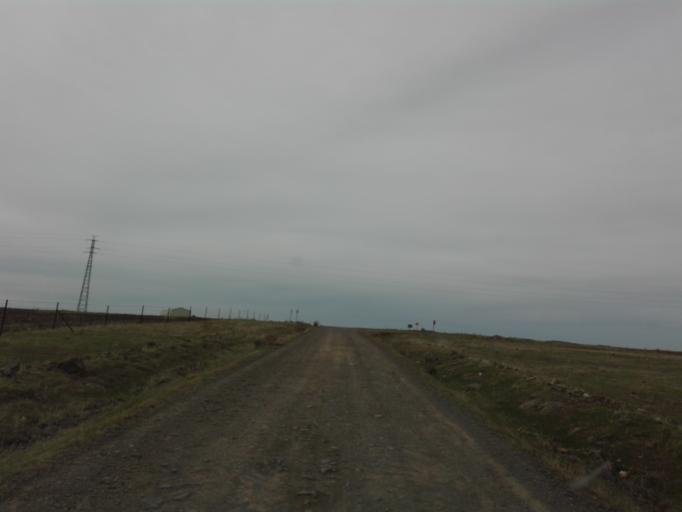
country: ES
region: Extremadura
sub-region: Provincia de Badajoz
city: Llerena
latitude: 38.2539
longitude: -6.0199
